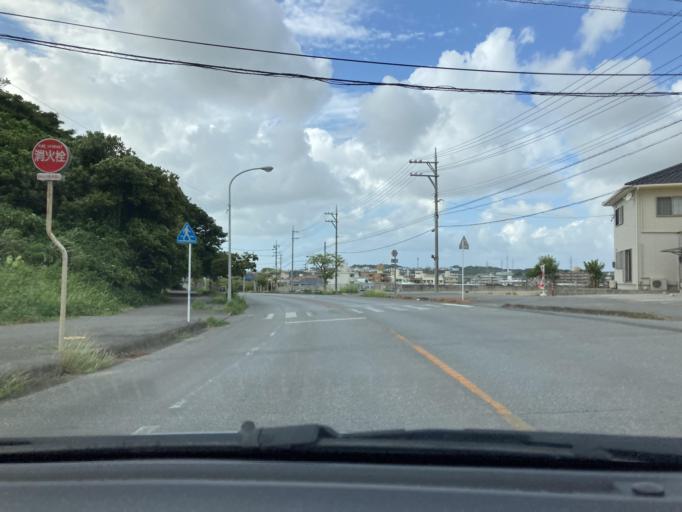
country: JP
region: Okinawa
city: Itoman
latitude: 26.1298
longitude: 127.6889
